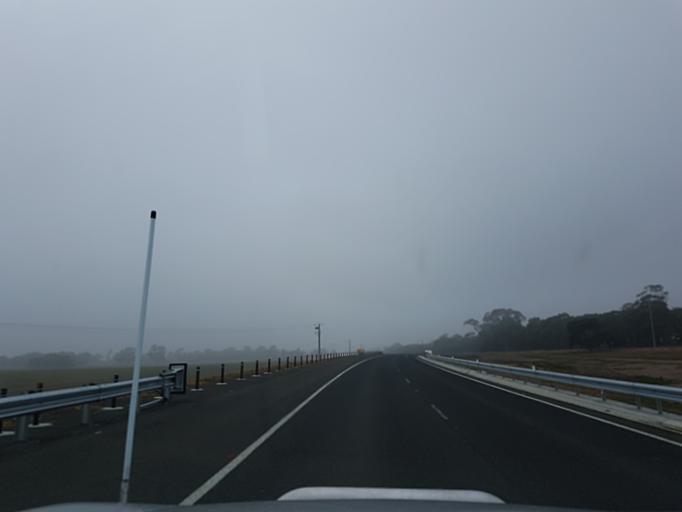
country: AU
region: Victoria
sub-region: Latrobe
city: Traralgon
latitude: -38.1796
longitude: 146.6195
